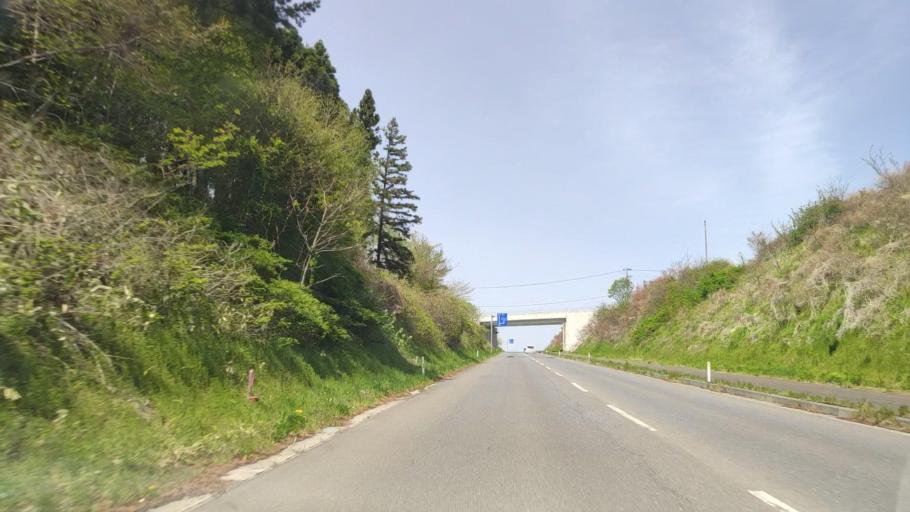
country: JP
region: Aomori
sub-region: Hachinohe Shi
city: Uchimaru
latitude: 40.5256
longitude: 141.4119
